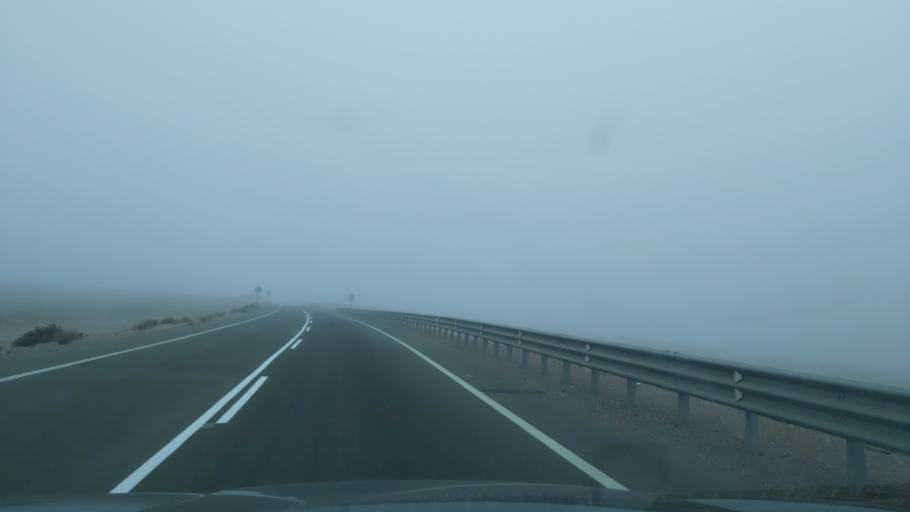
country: CL
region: Atacama
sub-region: Provincia de Copiapo
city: Copiapo
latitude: -27.2783
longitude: -70.0862
